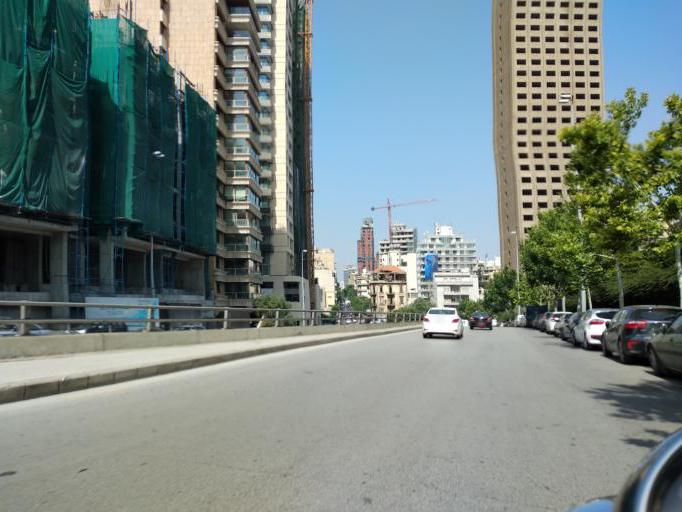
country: LB
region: Beyrouth
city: Beirut
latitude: 33.8949
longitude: 35.4981
